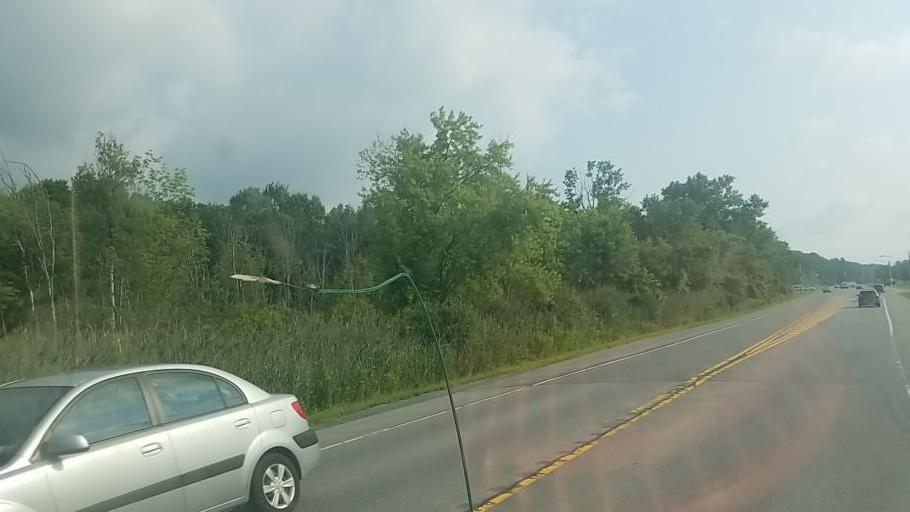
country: US
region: New York
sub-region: Fulton County
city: Gloversville
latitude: 43.0319
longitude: -74.3464
